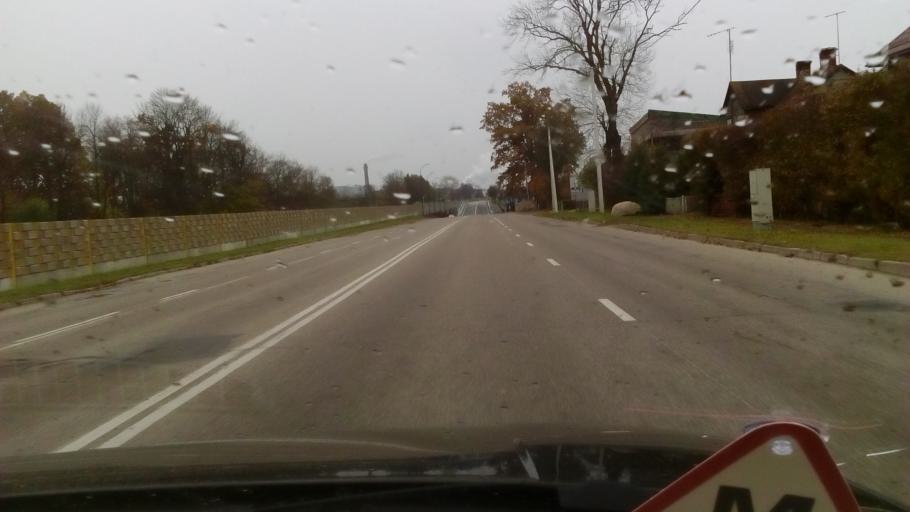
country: LT
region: Marijampoles apskritis
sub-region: Marijampole Municipality
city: Marijampole
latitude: 54.5472
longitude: 23.3575
